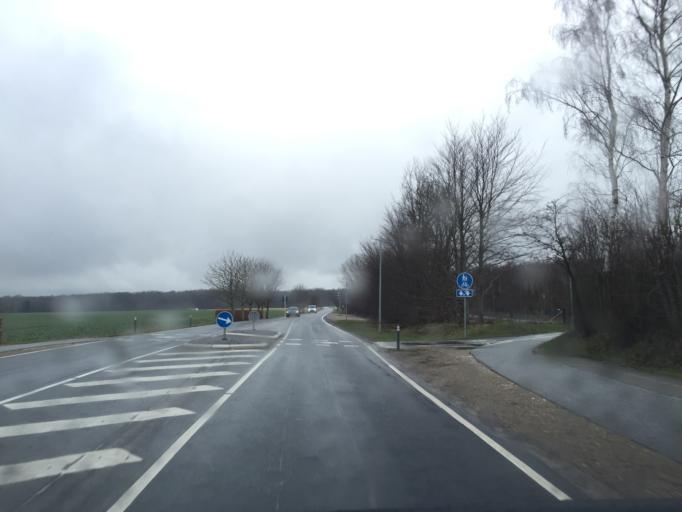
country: DK
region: Capital Region
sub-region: Fureso Kommune
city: Farum
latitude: 55.8145
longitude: 12.3444
